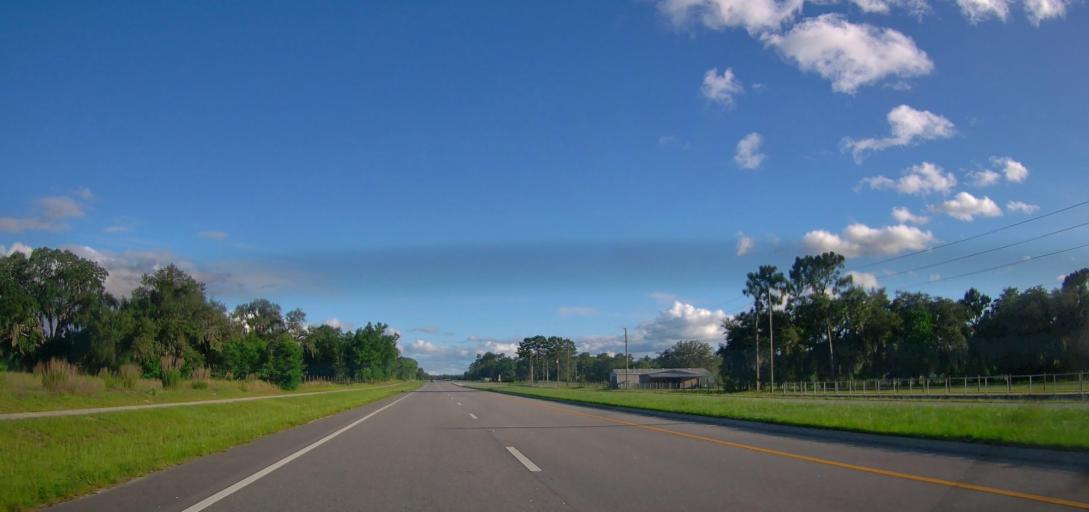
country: US
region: Florida
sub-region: Marion County
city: Belleview
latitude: 29.0483
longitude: -82.0174
